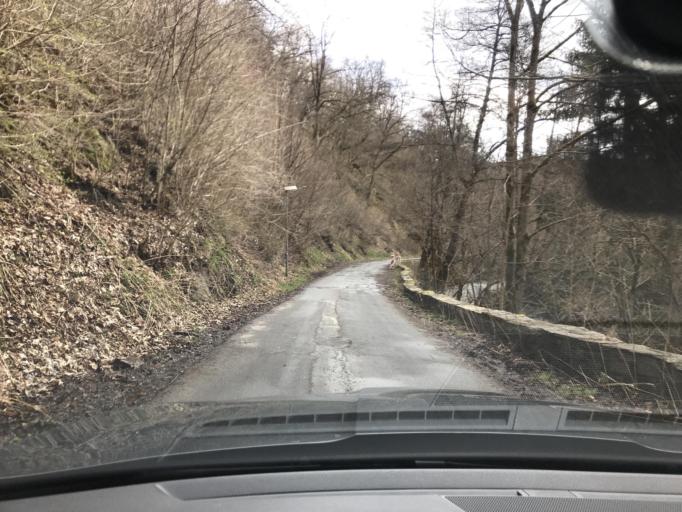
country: DE
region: Saxony-Anhalt
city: Harzgerode
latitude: 51.6664
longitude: 11.1431
